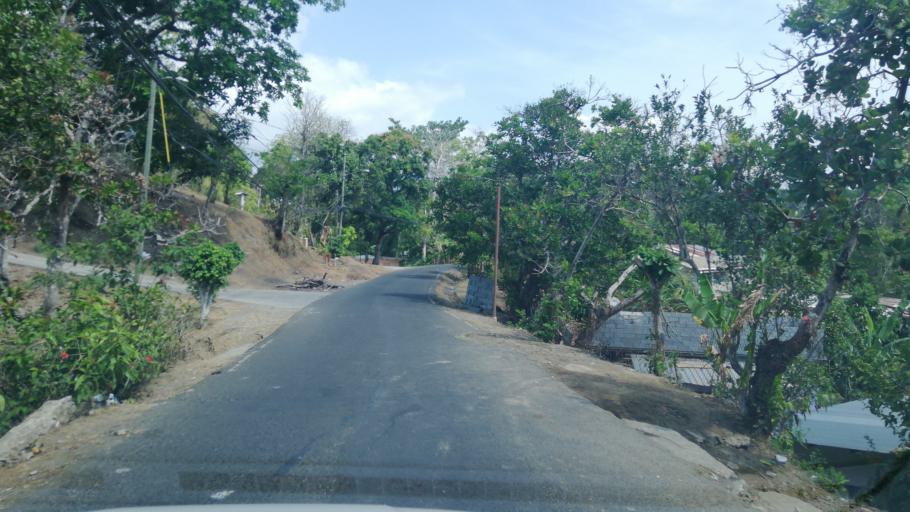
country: PA
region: Panama
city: Alcalde Diaz
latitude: 9.1220
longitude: -79.5644
